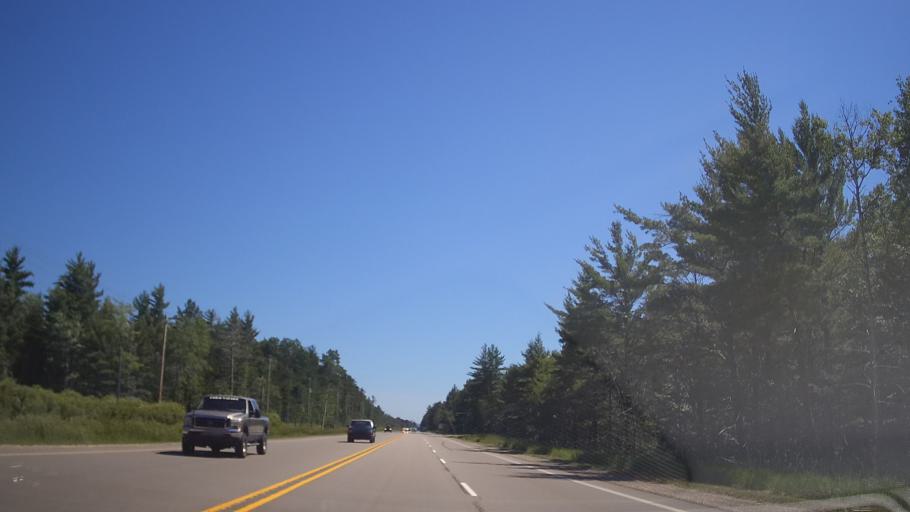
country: US
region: Michigan
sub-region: Cheboygan County
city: Indian River
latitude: 45.5243
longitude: -84.7817
